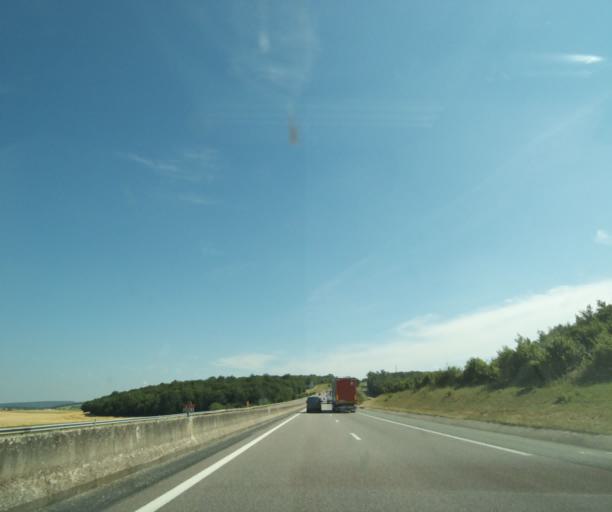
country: FR
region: Lorraine
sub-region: Departement de Meurthe-et-Moselle
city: Colombey-les-Belles
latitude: 48.4598
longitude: 5.8700
